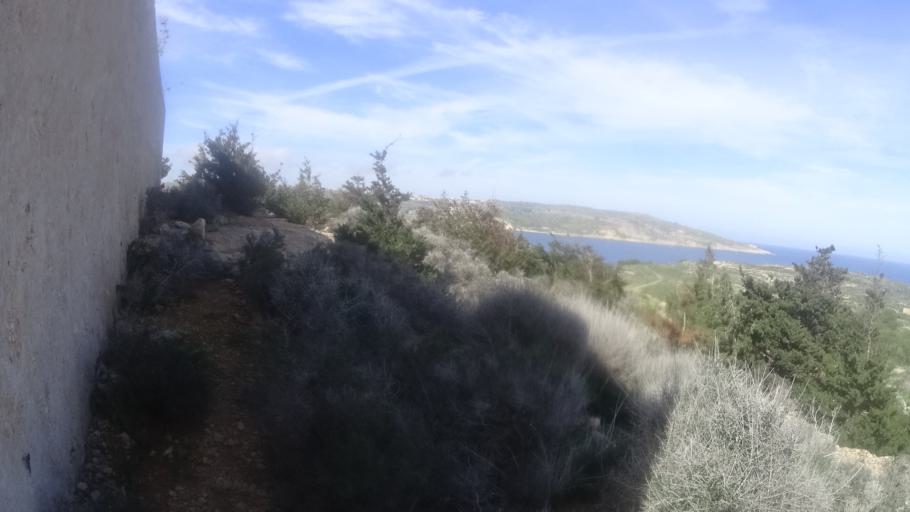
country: MT
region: Il-Qala
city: Qala
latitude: 36.0121
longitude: 14.3310
